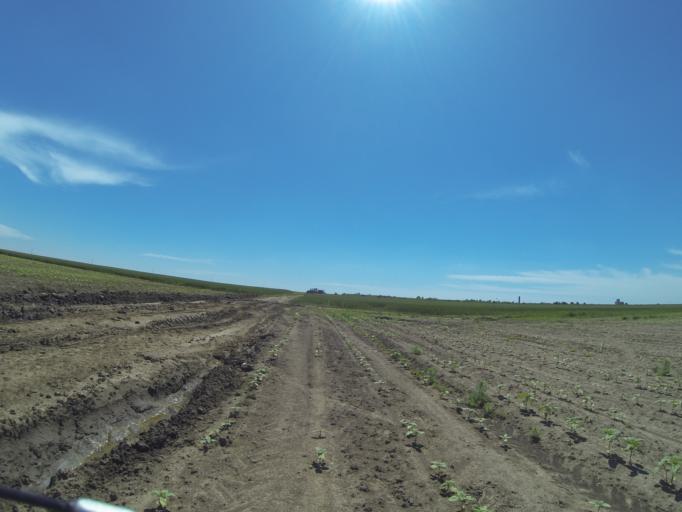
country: RO
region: Dolj
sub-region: Comuna Dragotesti
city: Dragotesti
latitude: 44.2048
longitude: 24.0670
